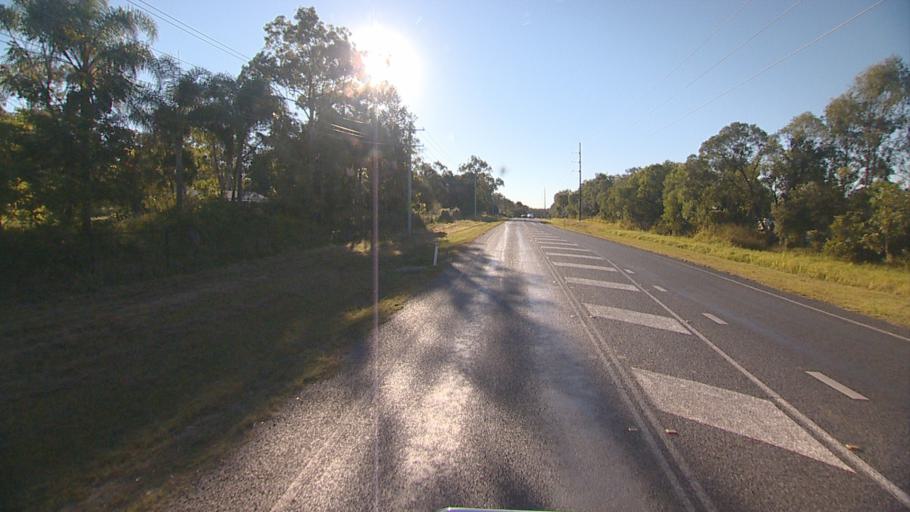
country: AU
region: Queensland
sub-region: Logan
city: Chambers Flat
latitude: -27.7488
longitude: 153.0914
